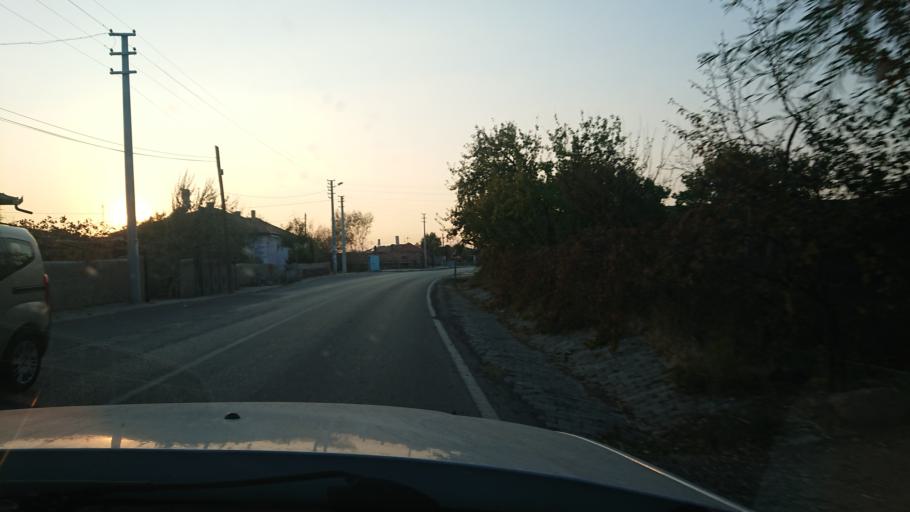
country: TR
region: Aksaray
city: Aksaray
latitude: 38.2993
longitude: 34.0744
